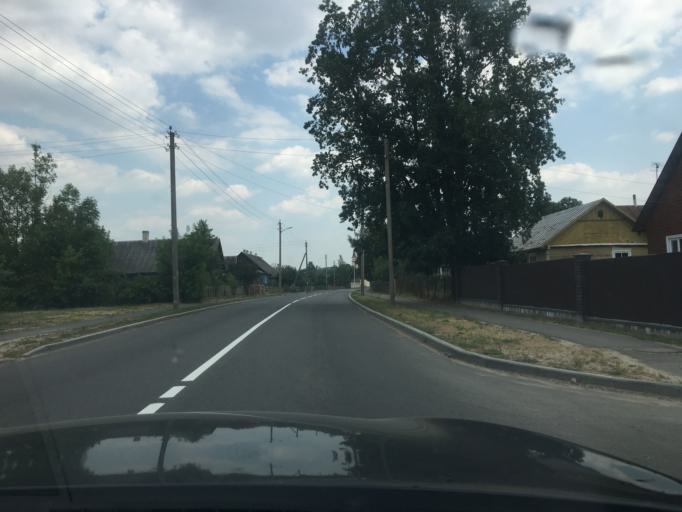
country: BY
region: Brest
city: Ruzhany
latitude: 52.8672
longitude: 24.8787
